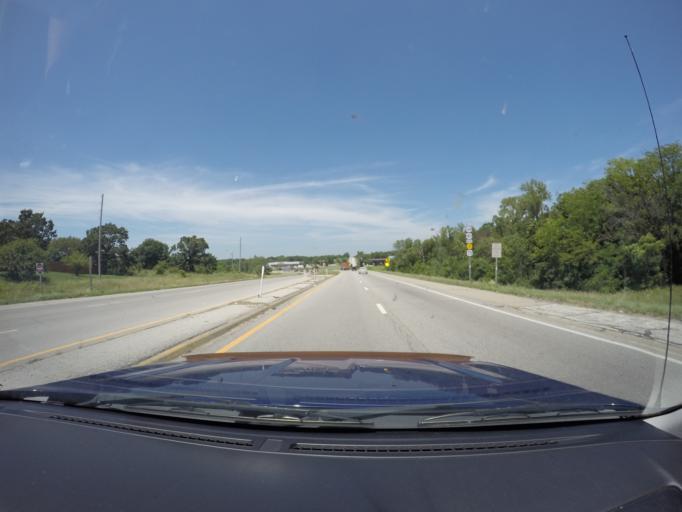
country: US
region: Kansas
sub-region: Wyandotte County
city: Bonner Springs
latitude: 39.1018
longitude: -94.8817
